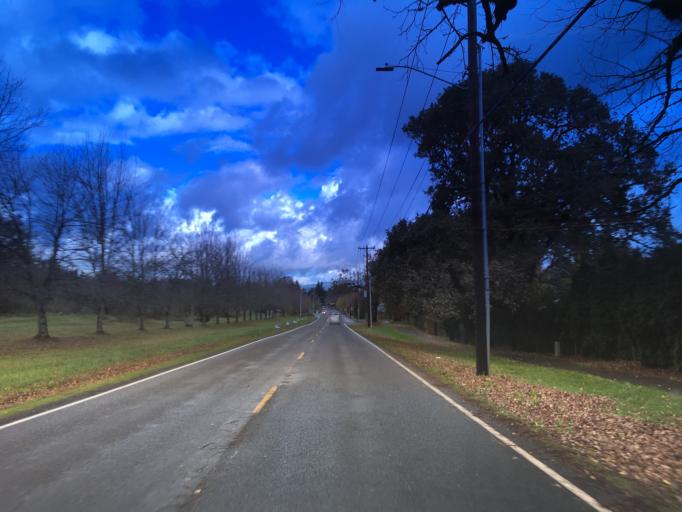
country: US
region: Oregon
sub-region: Multnomah County
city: Troutdale
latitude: 45.5147
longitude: -122.3871
